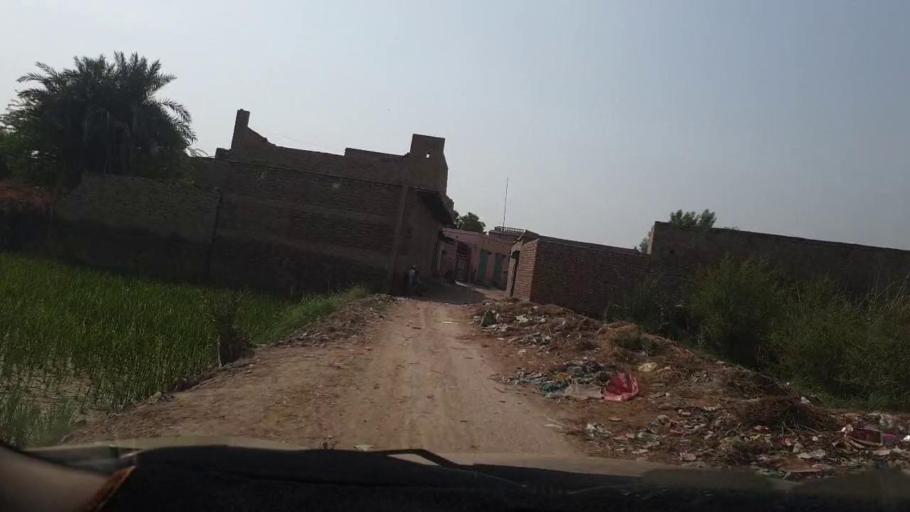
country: PK
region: Sindh
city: Goth Garelo
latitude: 27.4341
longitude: 68.0439
